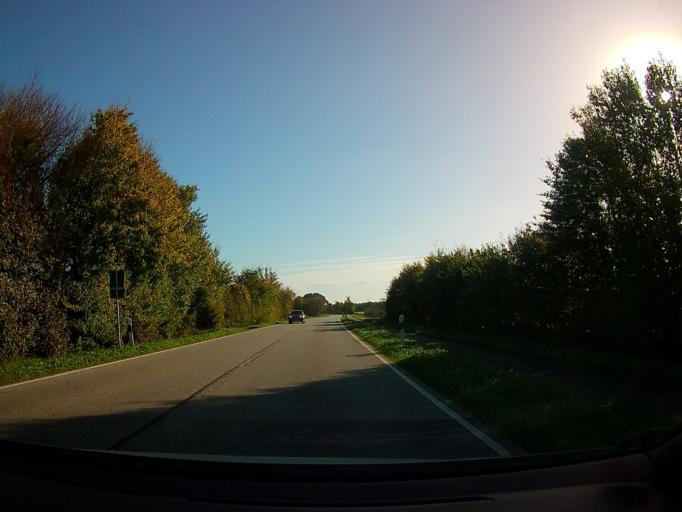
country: DE
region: Schleswig-Holstein
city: Silberstedt
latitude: 54.5177
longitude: 9.4009
